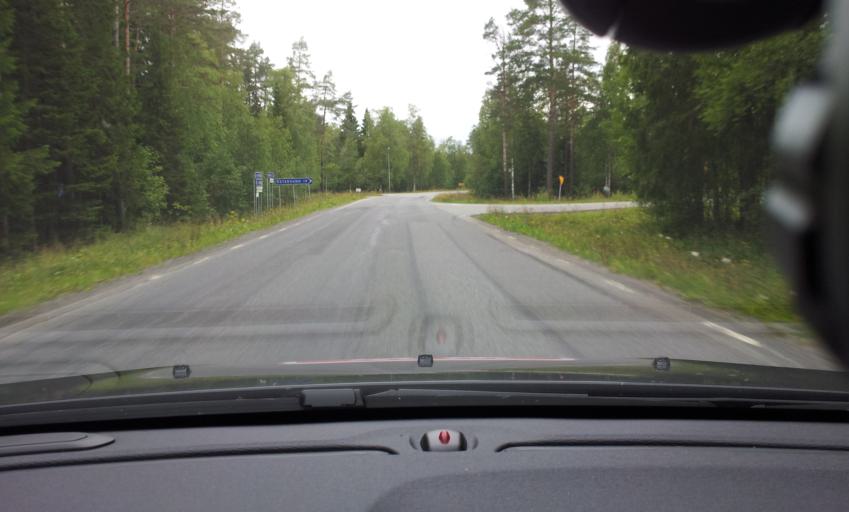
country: SE
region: Jaemtland
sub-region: OEstersunds Kommun
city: Brunflo
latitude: 63.0479
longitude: 14.8619
